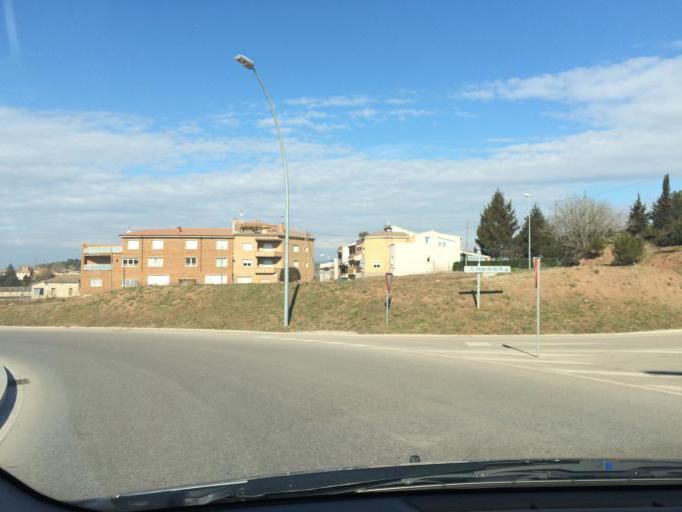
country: ES
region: Catalonia
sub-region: Provincia de Barcelona
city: Manresa
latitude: 41.7391
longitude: 1.8227
